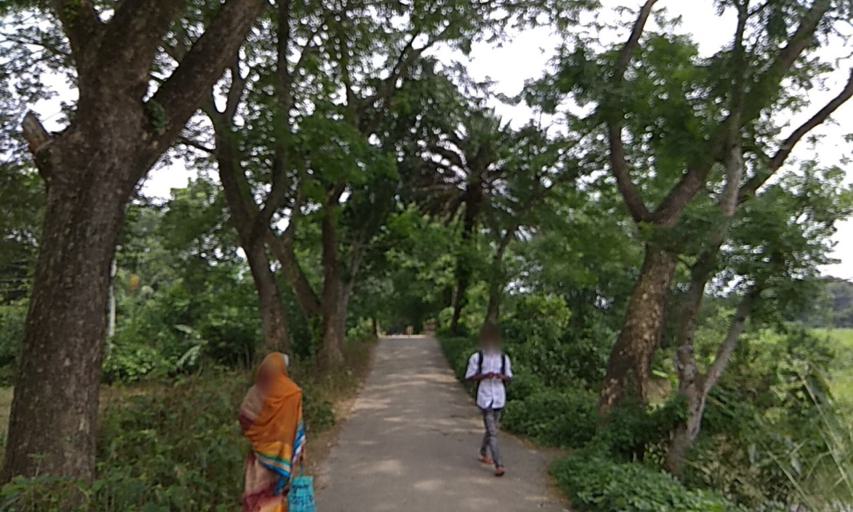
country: BD
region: Dhaka
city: Faridpur
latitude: 23.5354
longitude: 89.9689
